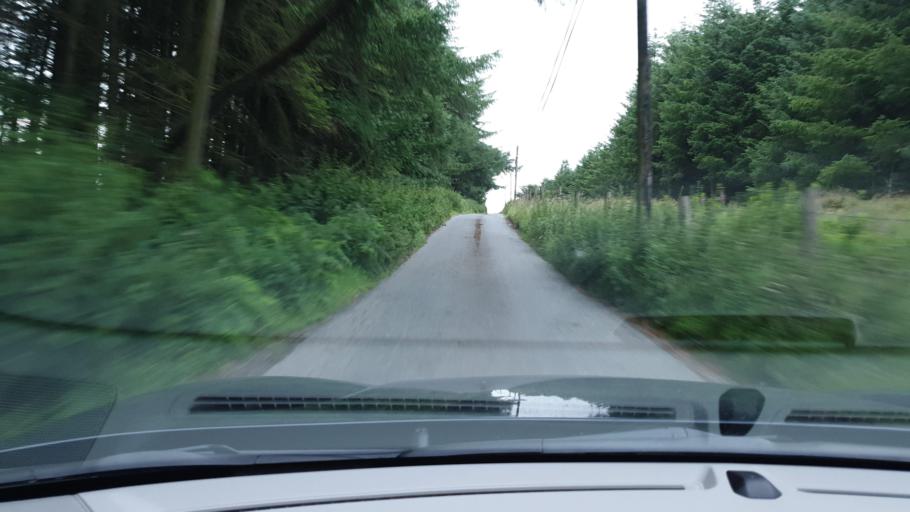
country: IE
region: Leinster
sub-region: Wicklow
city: Blessington
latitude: 53.2218
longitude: -6.4946
